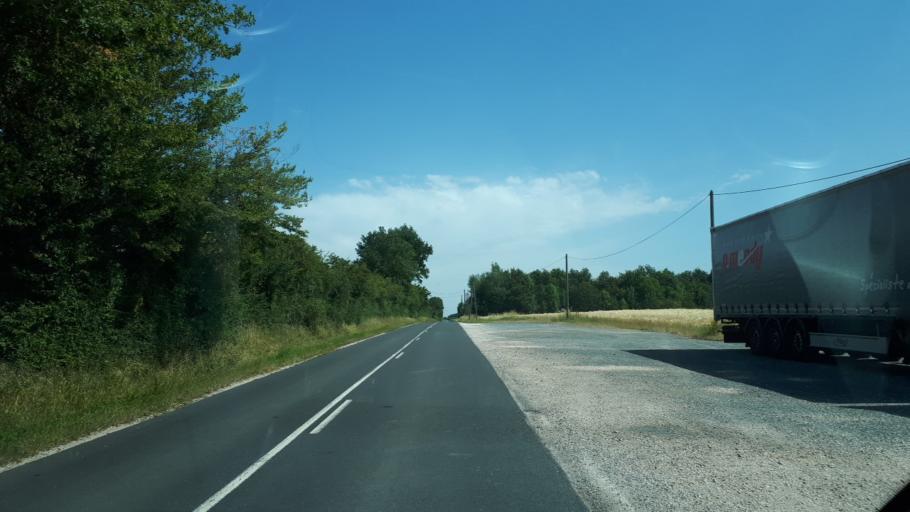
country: FR
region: Centre
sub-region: Departement du Loir-et-Cher
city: Droue
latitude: 47.9928
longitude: 1.0387
